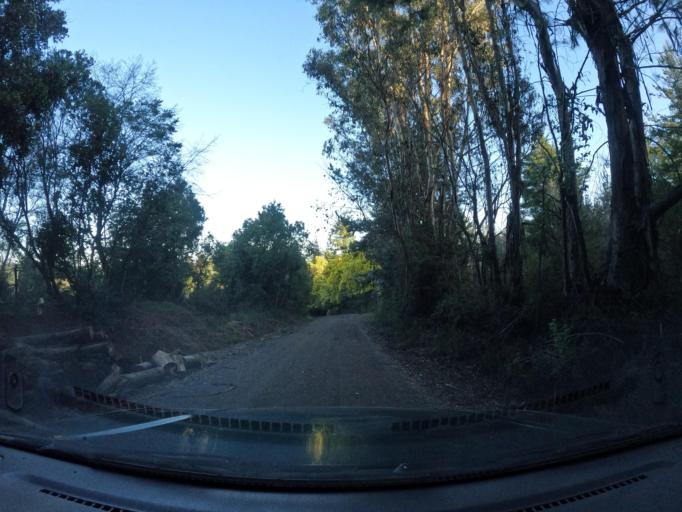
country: CL
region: Biobio
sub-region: Provincia de Concepcion
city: Chiguayante
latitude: -37.0153
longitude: -72.8411
